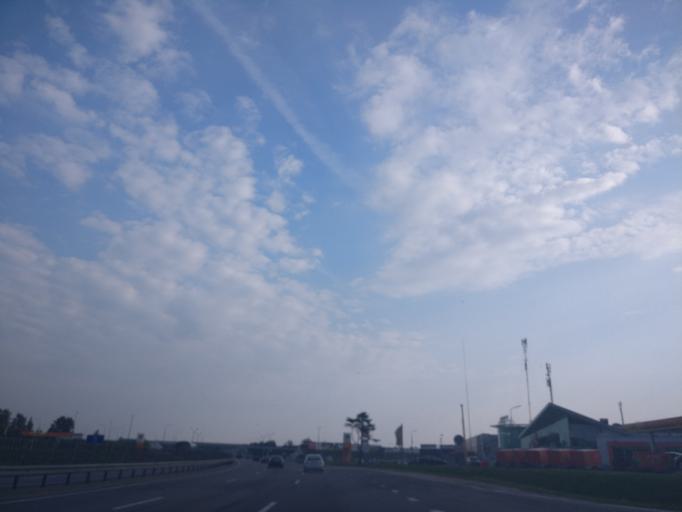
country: BY
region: Minsk
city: Borovlyany
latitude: 53.9640
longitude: 27.6423
